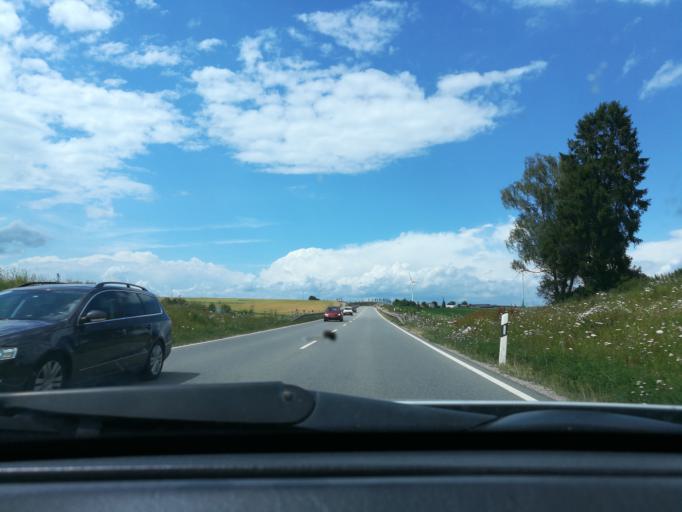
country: DE
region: Baden-Wuerttemberg
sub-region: Freiburg Region
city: Bosingen
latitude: 48.2082
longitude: 8.5378
